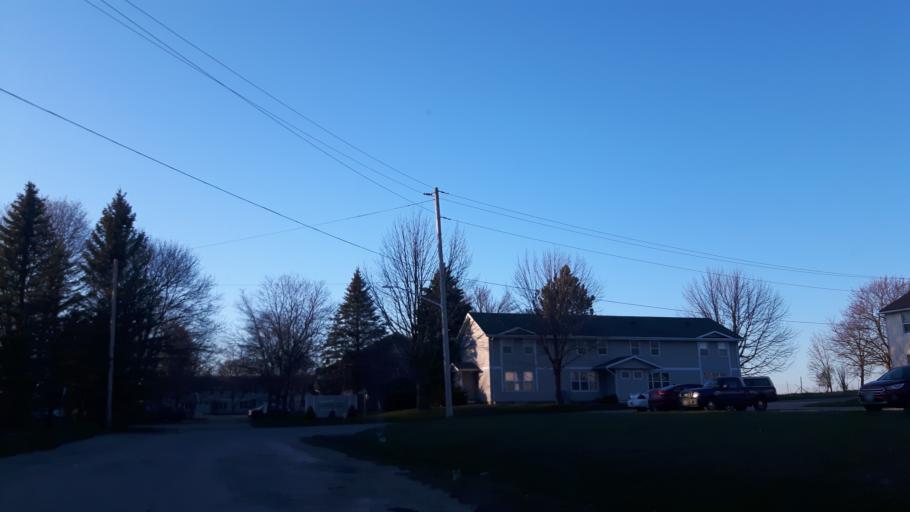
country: CA
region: Ontario
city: Bluewater
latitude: 43.5852
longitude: -81.5178
